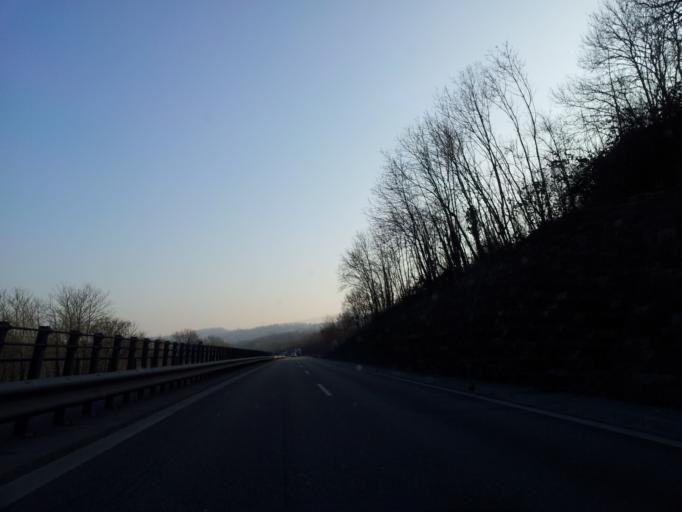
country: DE
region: Baden-Wuerttemberg
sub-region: Freiburg Region
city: Bad Bellingen
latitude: 47.7107
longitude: 7.5306
